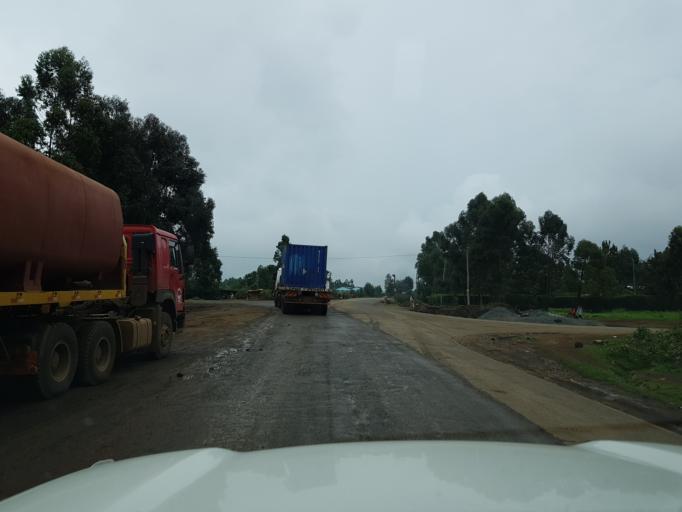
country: KE
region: Kiambu
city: Limuru
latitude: -1.1325
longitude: 36.6357
